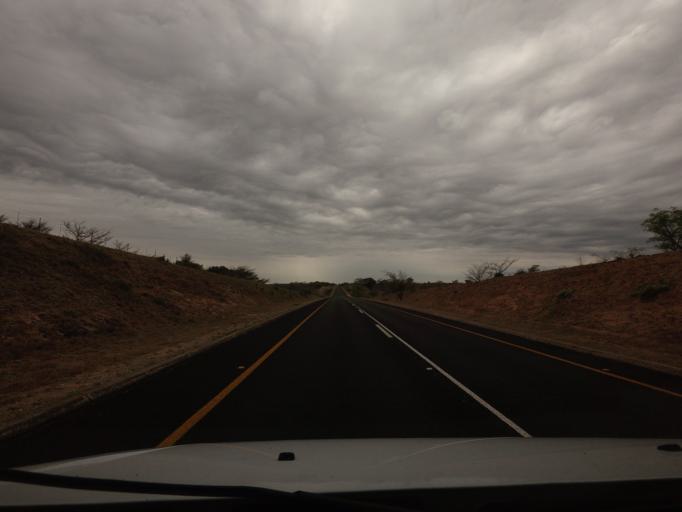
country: ZA
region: Limpopo
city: Thulamahashi
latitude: -24.5678
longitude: 31.0852
